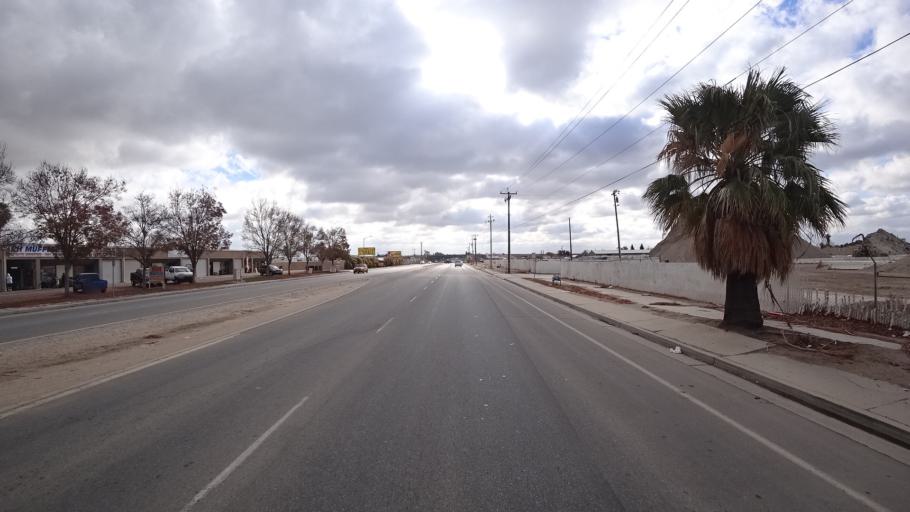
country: US
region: California
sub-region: Kern County
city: Bakersfield
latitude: 35.3566
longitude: -118.9676
